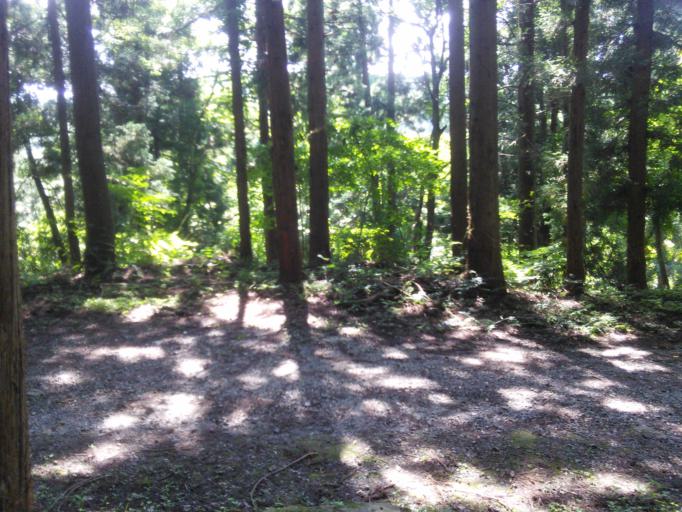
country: JP
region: Fukushima
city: Inawashiro
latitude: 37.5121
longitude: 139.9806
